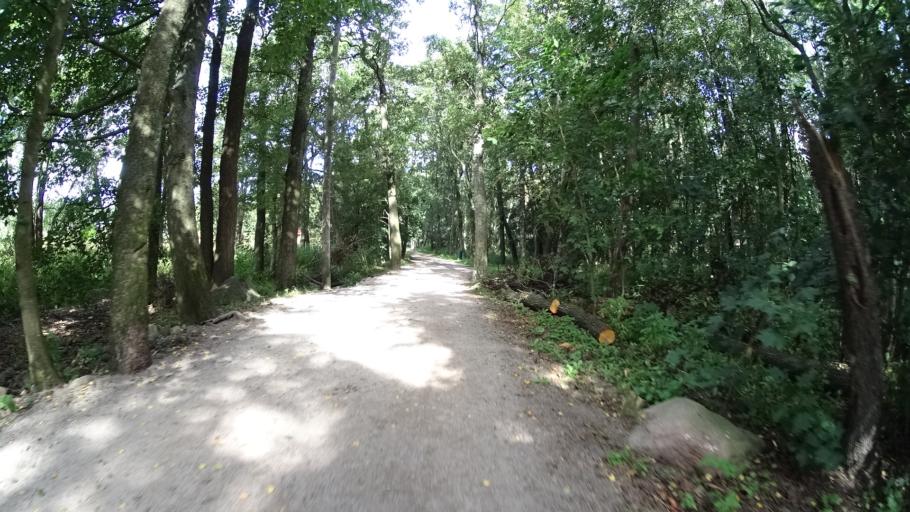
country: FI
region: Uusimaa
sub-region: Helsinki
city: Teekkarikylae
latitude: 60.1532
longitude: 24.8748
